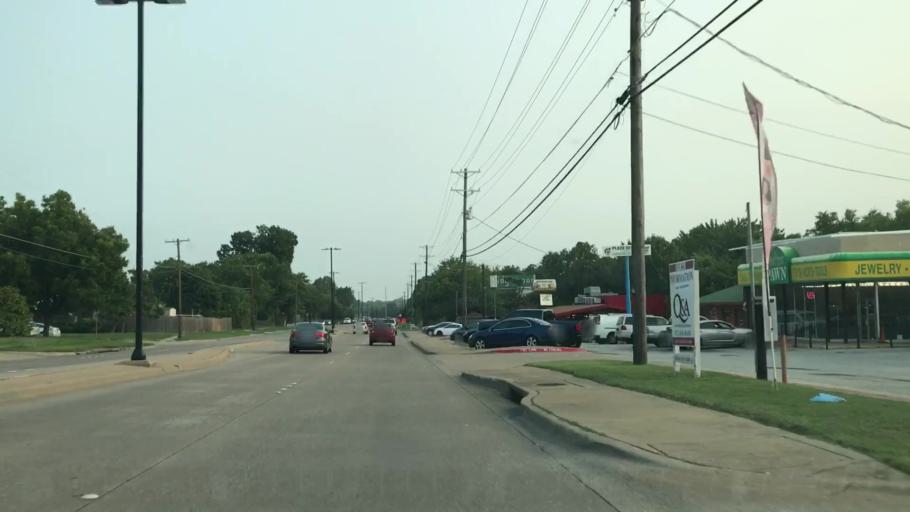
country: US
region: Texas
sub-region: Dallas County
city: Garland
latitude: 32.8776
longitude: -96.6310
